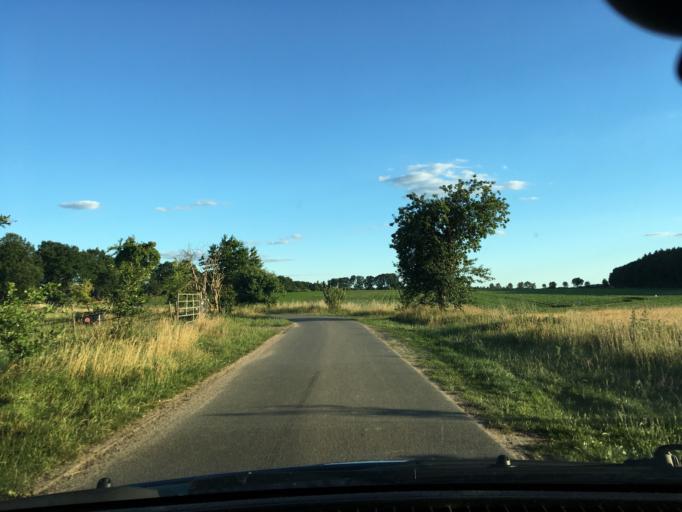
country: DE
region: Lower Saxony
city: Egestorf
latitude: 53.1930
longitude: 10.0978
